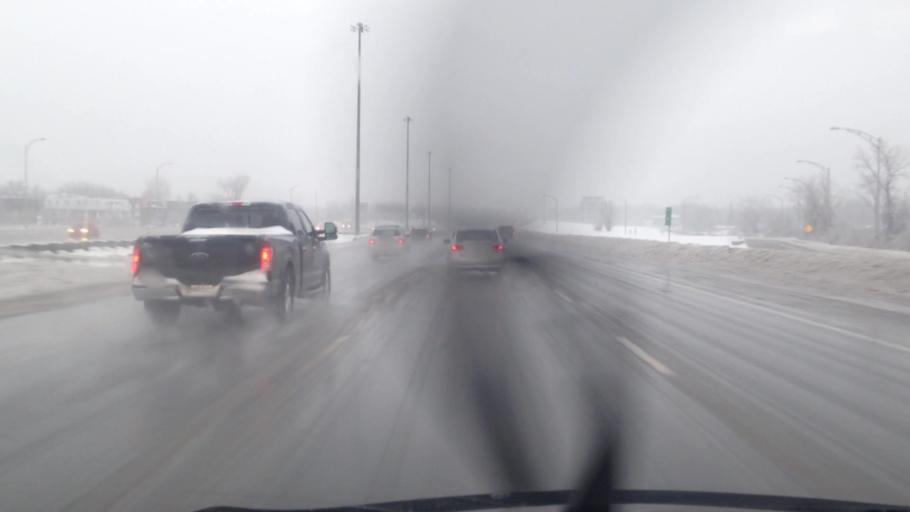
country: CA
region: Quebec
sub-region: Laurentides
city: Boisbriand
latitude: 45.6186
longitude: -73.8266
